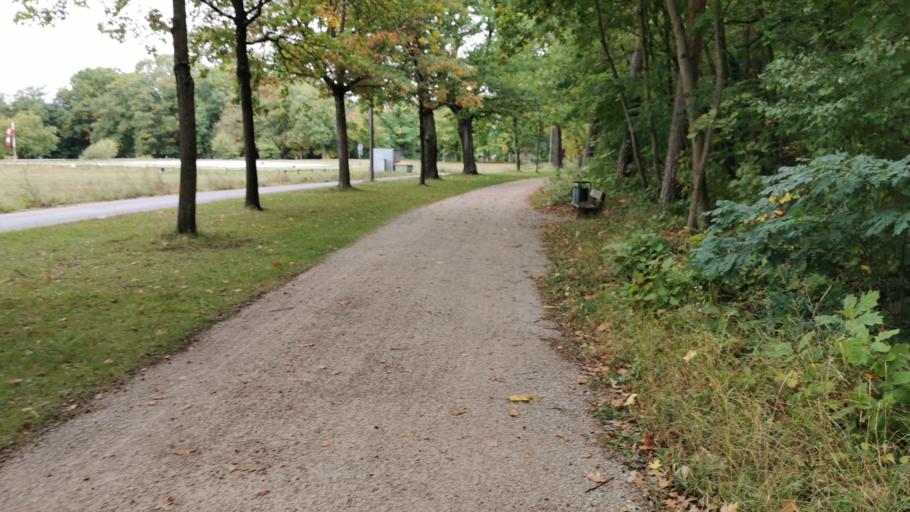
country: DE
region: Bavaria
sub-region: Regierungsbezirk Mittelfranken
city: Erlangen
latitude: 49.6021
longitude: 11.0236
